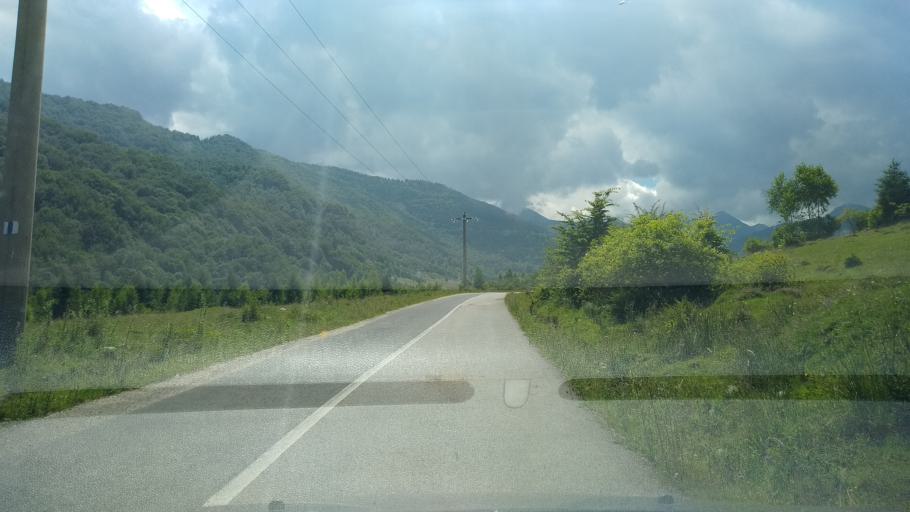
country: RO
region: Hunedoara
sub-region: Comuna Rau de Mori
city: Rau de Mori
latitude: 45.4617
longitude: 22.8980
